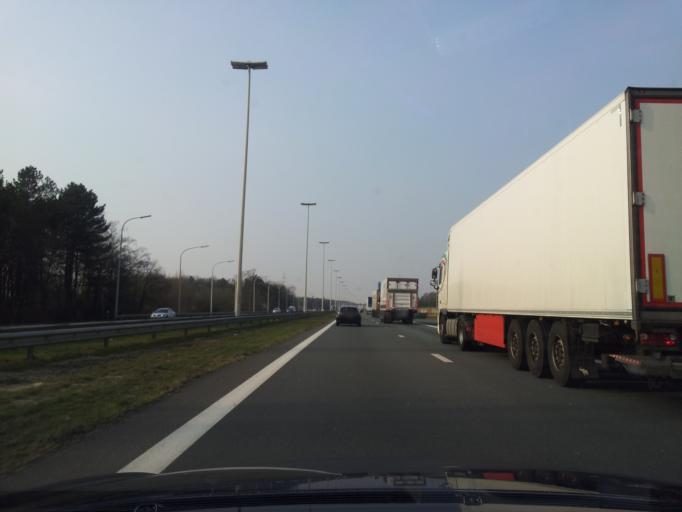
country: BE
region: Flanders
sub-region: Provincie Antwerpen
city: Schilde
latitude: 51.3138
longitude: 4.5672
